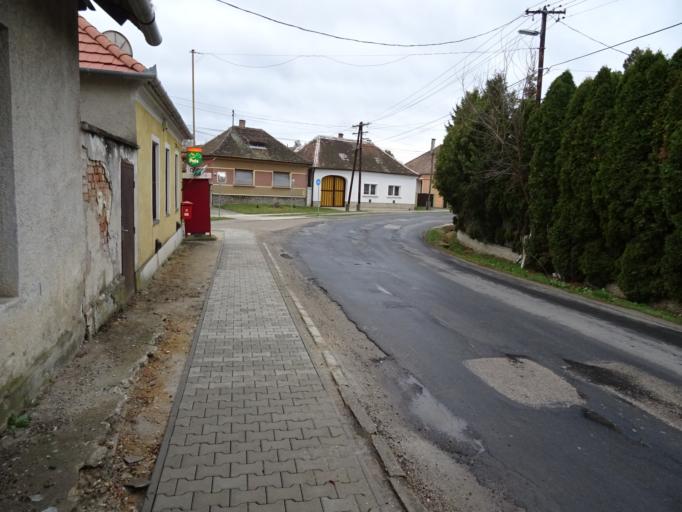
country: AT
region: Burgenland
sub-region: Politischer Bezirk Oberpullendorf
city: Lutzmannsburg
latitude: 47.4584
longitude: 16.6756
